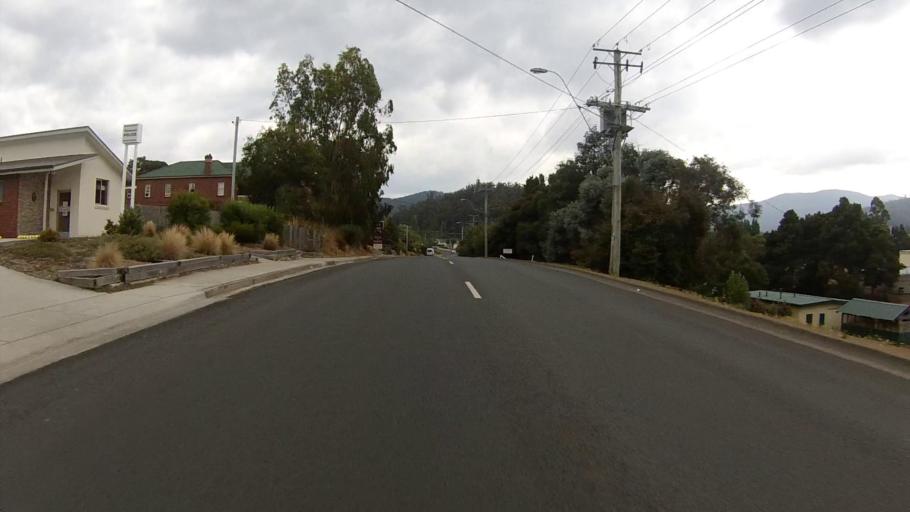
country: AU
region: Tasmania
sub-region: Huon Valley
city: Cygnet
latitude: -43.1574
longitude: 147.0745
